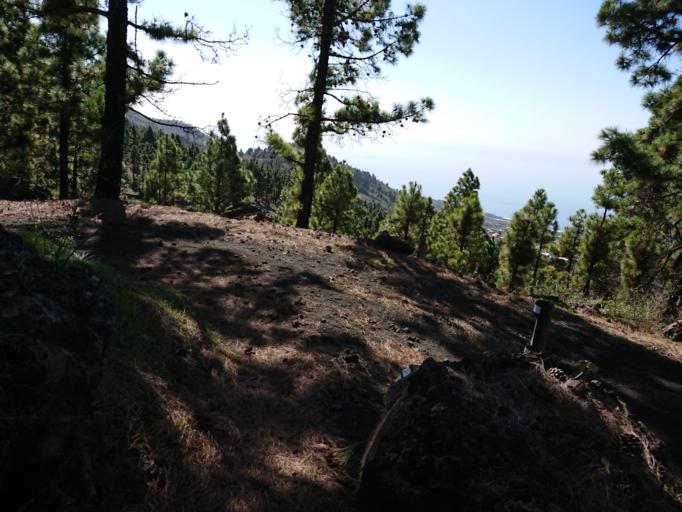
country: ES
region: Canary Islands
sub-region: Provincia de Santa Cruz de Tenerife
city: El Paso
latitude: 28.6077
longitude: -17.8673
